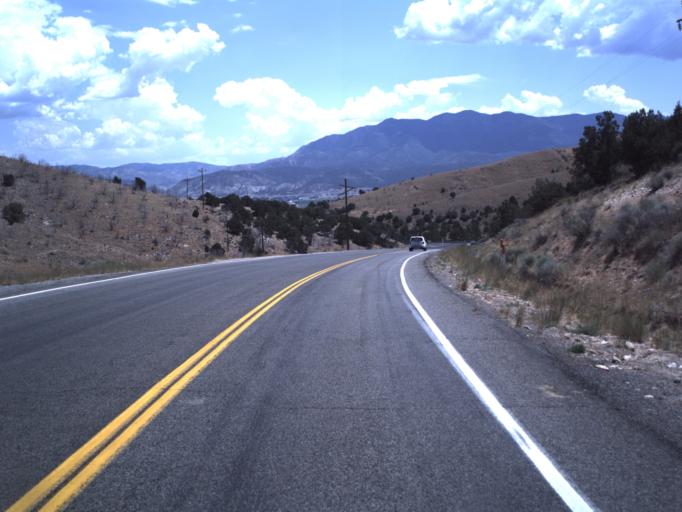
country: US
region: Utah
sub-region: Juab County
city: Nephi
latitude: 39.6982
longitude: -111.9463
